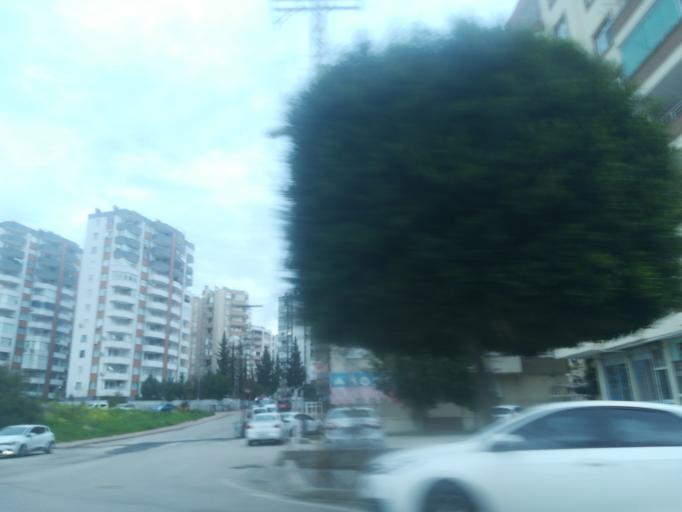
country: TR
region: Adana
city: Adana
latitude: 37.0412
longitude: 35.2923
